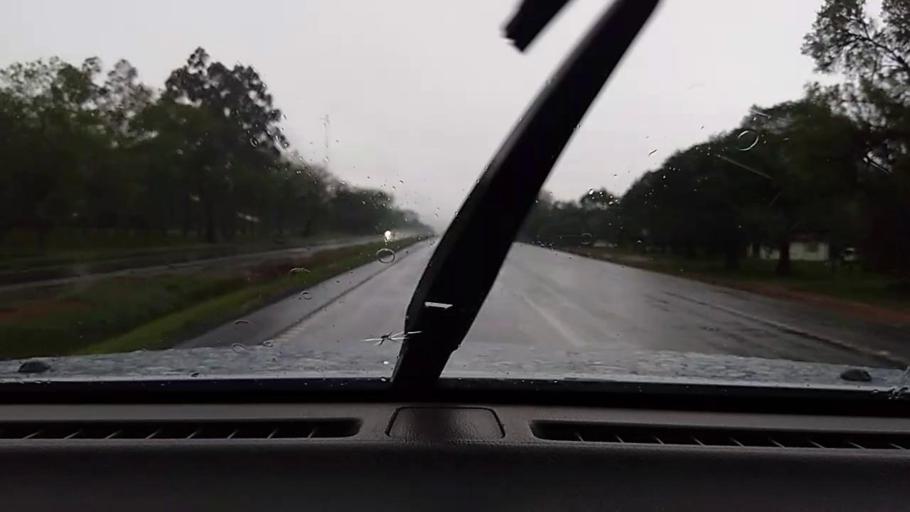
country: PY
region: Caaguazu
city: Repatriacion
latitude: -25.4518
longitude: -55.9036
